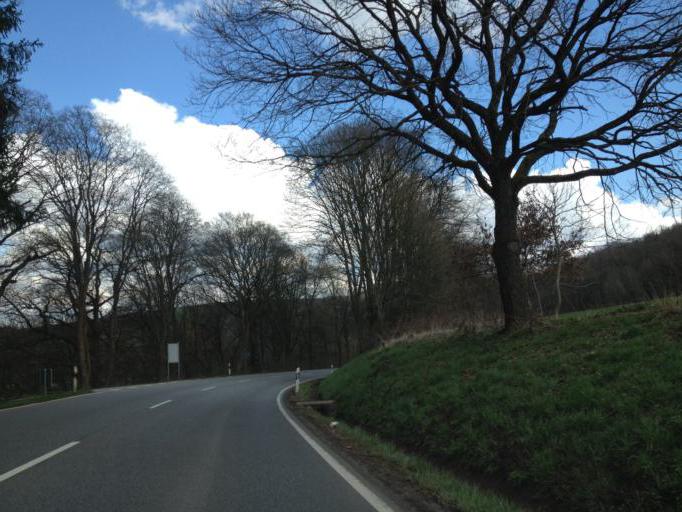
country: DE
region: Rheinland-Pfalz
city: Breitenbach
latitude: 49.4384
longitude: 7.2364
